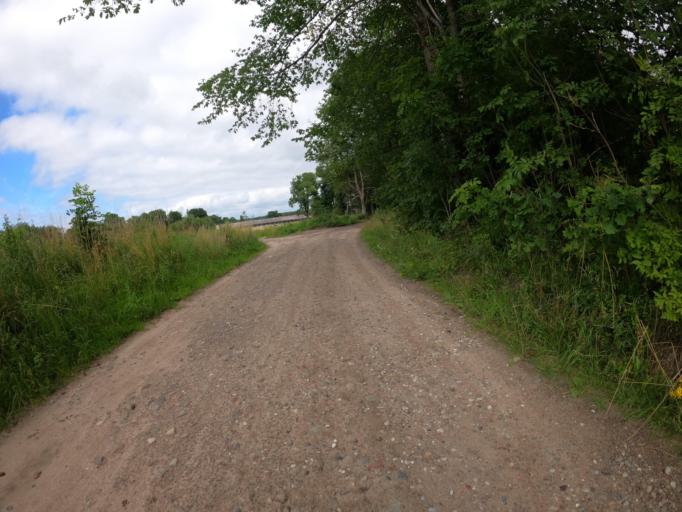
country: PL
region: West Pomeranian Voivodeship
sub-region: Powiat bialogardzki
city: Tychowo
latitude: 54.0006
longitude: 16.3729
